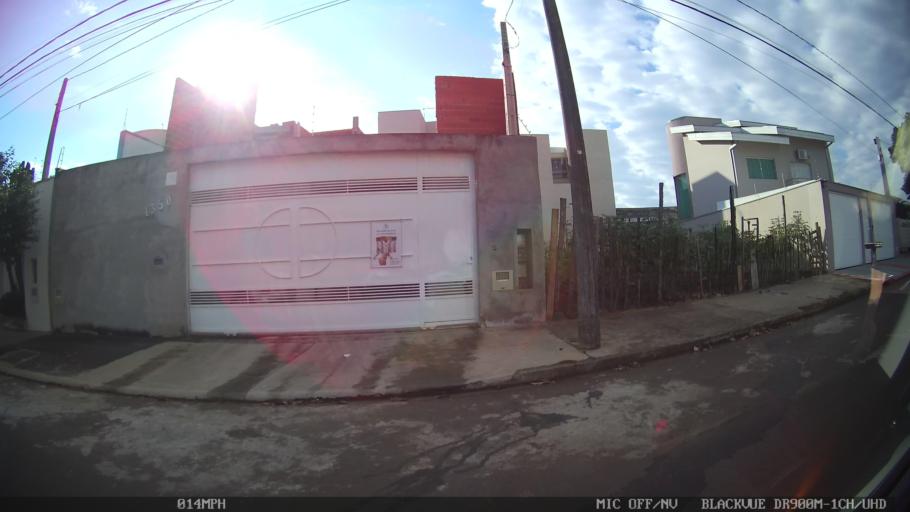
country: BR
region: Sao Paulo
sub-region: Americana
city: Americana
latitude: -22.7320
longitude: -47.3606
